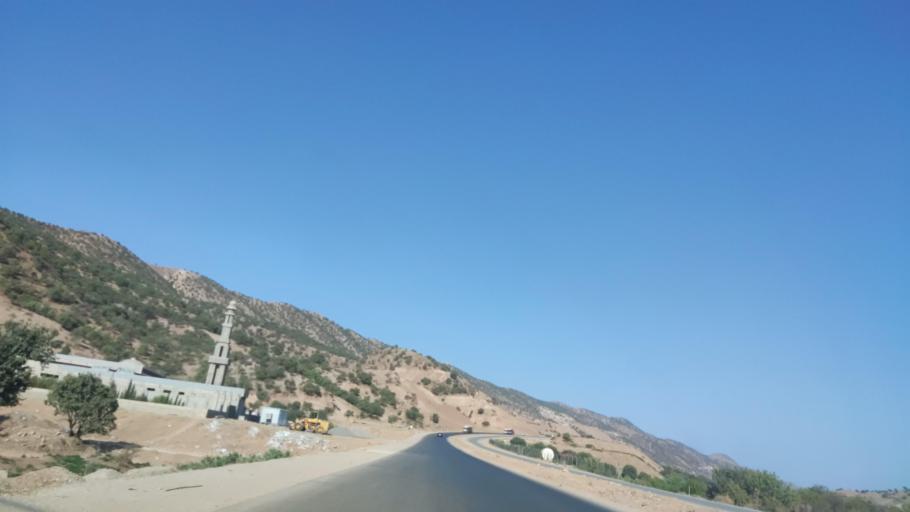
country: IQ
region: Arbil
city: Shaqlawah
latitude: 36.4309
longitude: 44.3180
